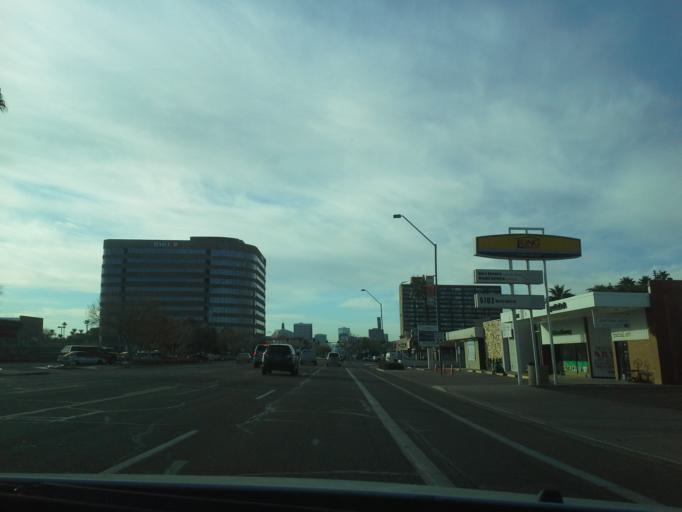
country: US
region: Arizona
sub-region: Maricopa County
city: Phoenix
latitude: 33.5115
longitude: -112.0739
